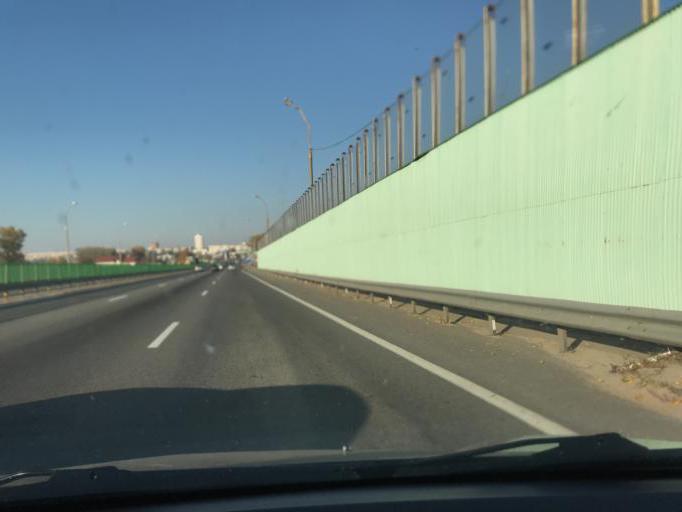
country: BY
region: Minsk
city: Syenitsa
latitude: 53.8281
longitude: 27.5341
